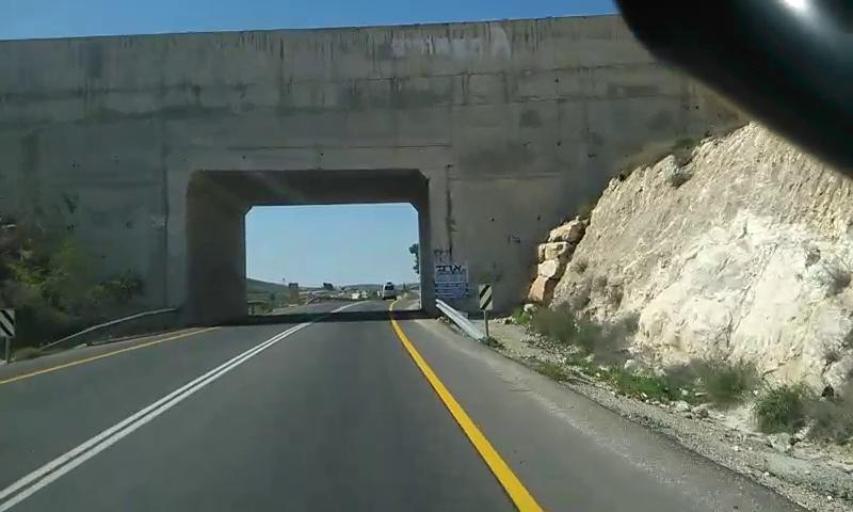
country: PS
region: West Bank
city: Bayt Ta`mar
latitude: 31.6708
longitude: 35.2396
